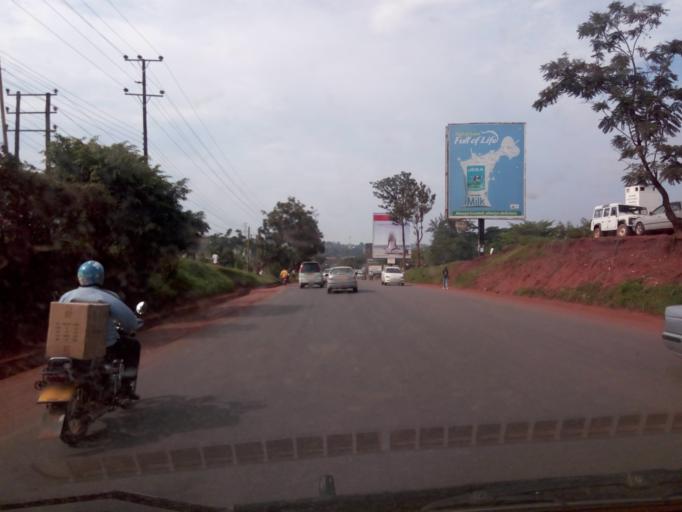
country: UG
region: Central Region
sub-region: Wakiso District
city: Kireka
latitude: 0.3320
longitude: 32.6160
